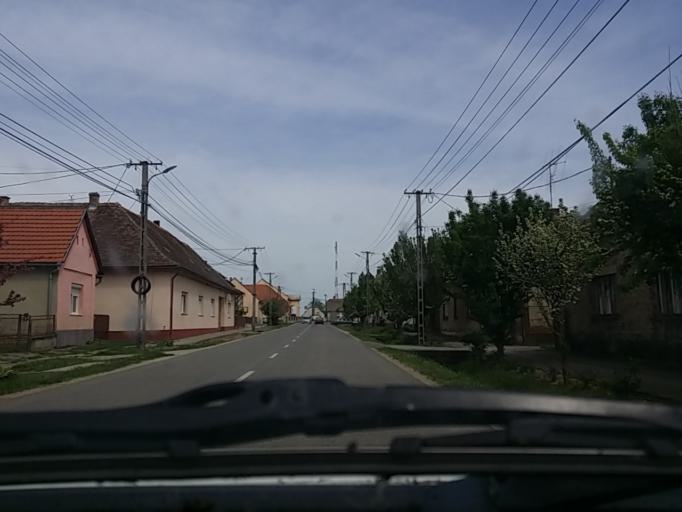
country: HU
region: Baranya
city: Sellye
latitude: 45.8738
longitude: 17.8418
